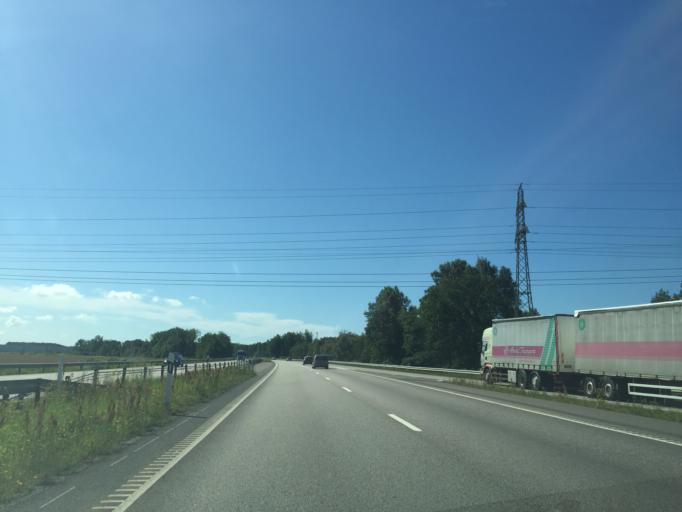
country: SE
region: Skane
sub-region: Helsingborg
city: Odakra
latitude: 56.0815
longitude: 12.7785
